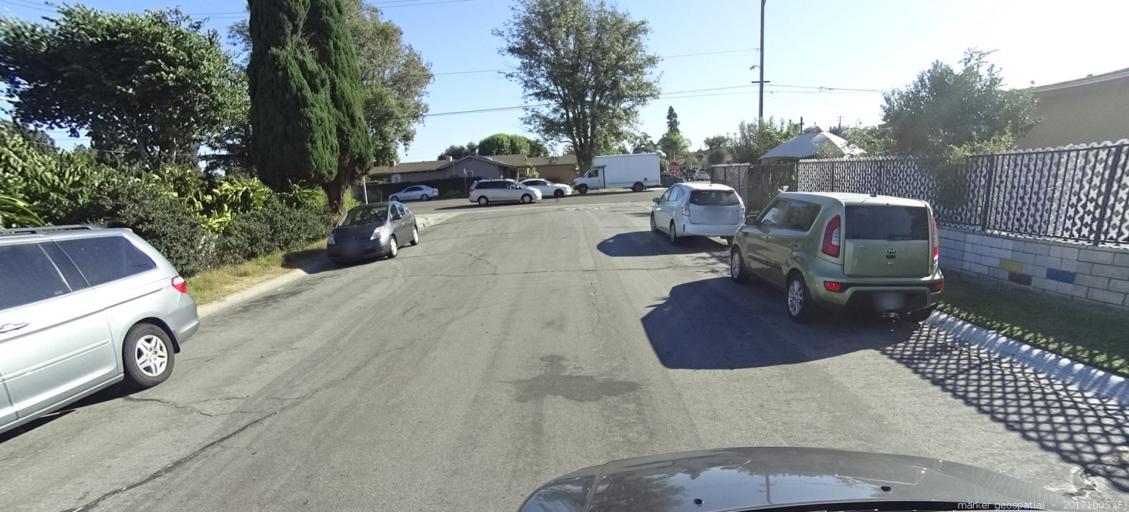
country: US
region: California
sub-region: Orange County
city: Stanton
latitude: 33.7889
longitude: -117.9711
